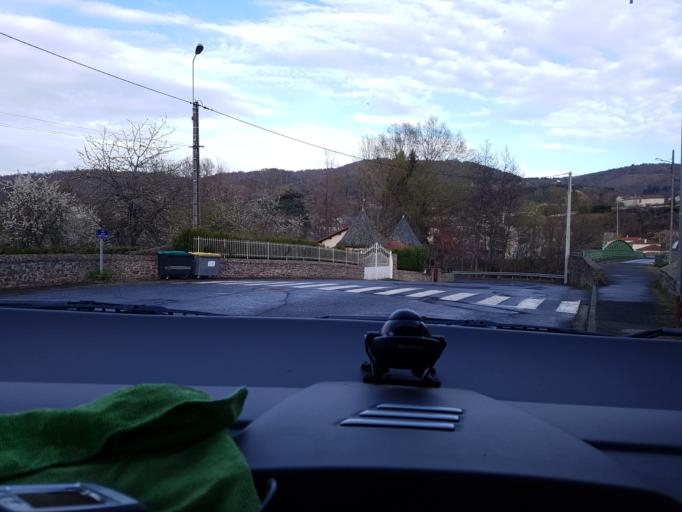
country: FR
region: Auvergne
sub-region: Departement du Cantal
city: Massiac
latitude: 45.2514
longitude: 3.1928
